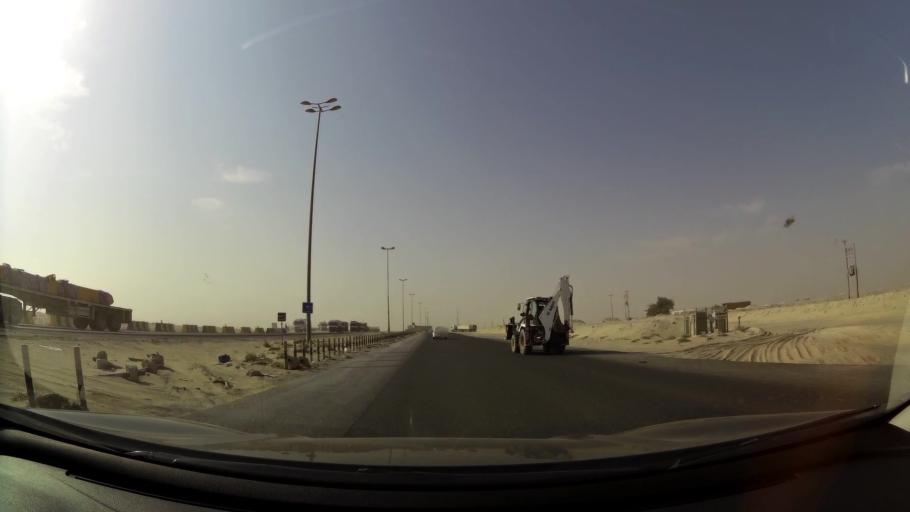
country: KW
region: Al Ahmadi
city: Al Ahmadi
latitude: 28.9154
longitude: 48.0988
